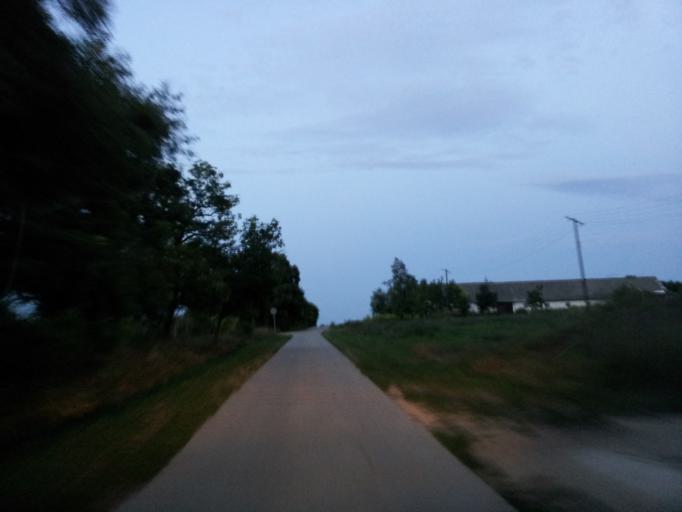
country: HU
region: Somogy
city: Zamardi
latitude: 46.8785
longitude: 17.9905
